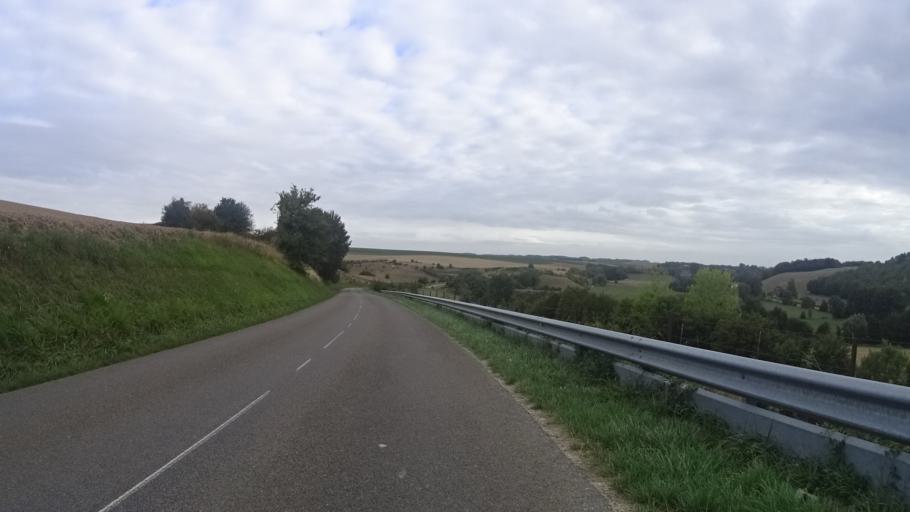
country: FR
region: Picardie
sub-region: Departement de l'Aisne
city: Guise
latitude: 49.9415
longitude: 3.5872
